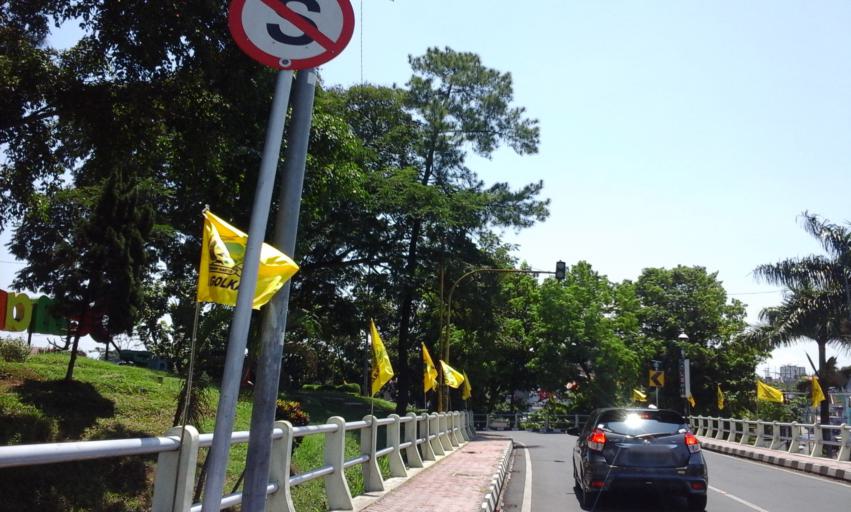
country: ID
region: East Java
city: Kepatihan
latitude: -8.1673
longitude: 113.7075
